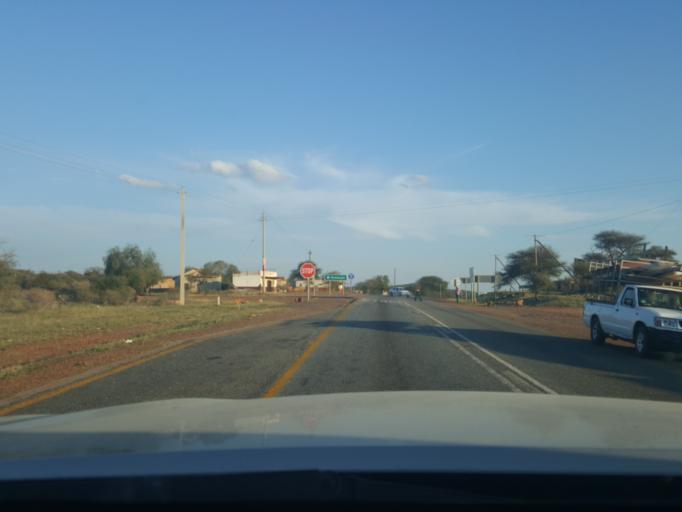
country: ZA
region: North-West
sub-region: Ngaka Modiri Molema District Municipality
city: Zeerust
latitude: -25.3855
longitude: 26.0842
